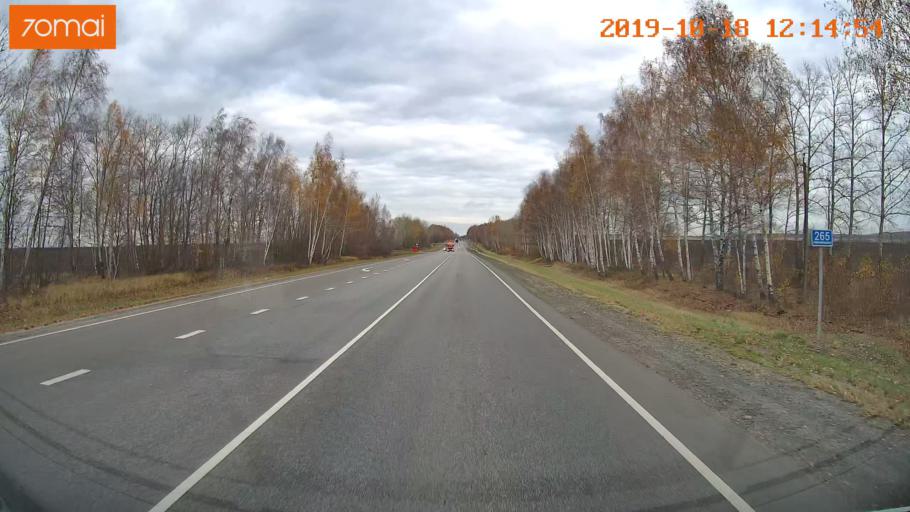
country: RU
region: Rjazan
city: Zakharovo
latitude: 54.4366
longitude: 39.3910
